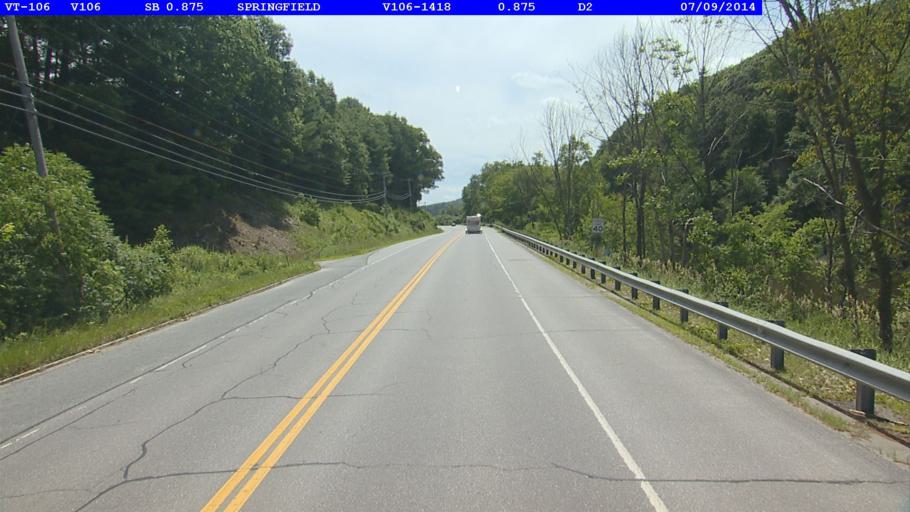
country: US
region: Vermont
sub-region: Windsor County
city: Springfield
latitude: 43.3142
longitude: -72.5015
